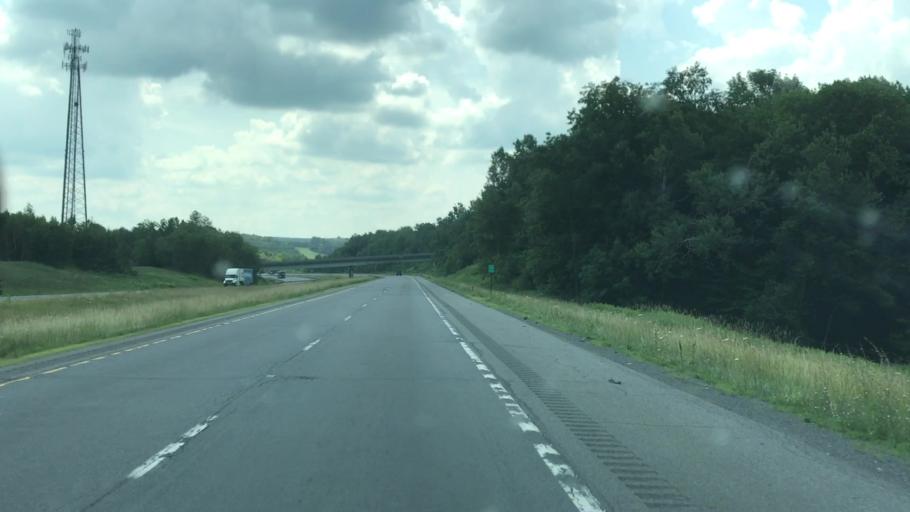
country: US
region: Pennsylvania
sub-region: Lackawanna County
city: Mount Cobb
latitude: 41.3740
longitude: -75.4513
